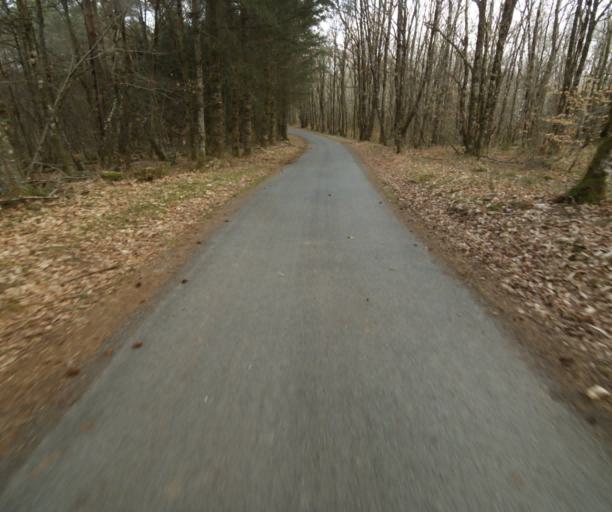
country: FR
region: Limousin
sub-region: Departement de la Correze
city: Correze
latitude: 45.2727
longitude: 1.9524
